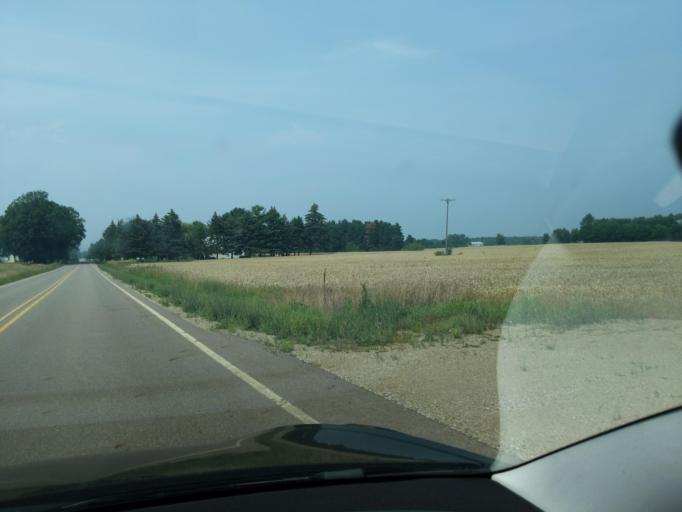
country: US
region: Michigan
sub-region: Clinton County
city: DeWitt
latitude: 42.8764
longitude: -84.5722
